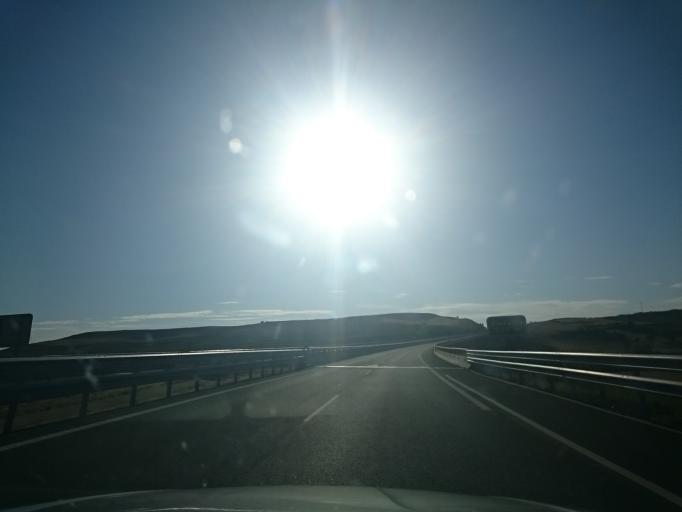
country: ES
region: Castille and Leon
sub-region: Provincia de Burgos
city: Villanueva de Argano
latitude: 42.3752
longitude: -3.9281
